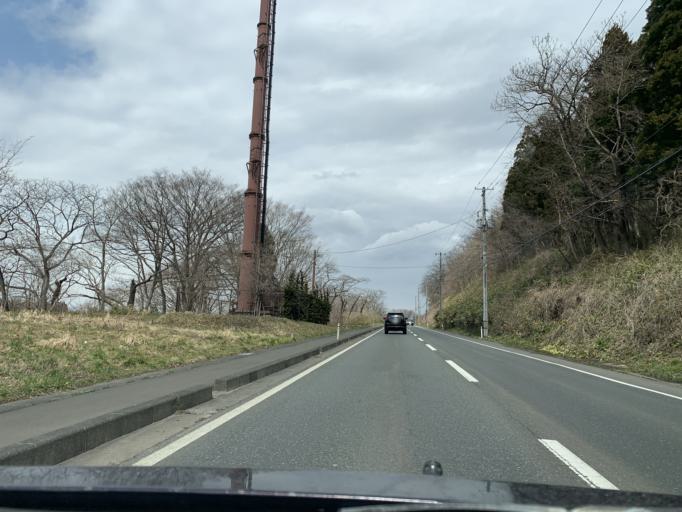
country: JP
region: Iwate
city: Kitakami
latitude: 39.2612
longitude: 141.1232
